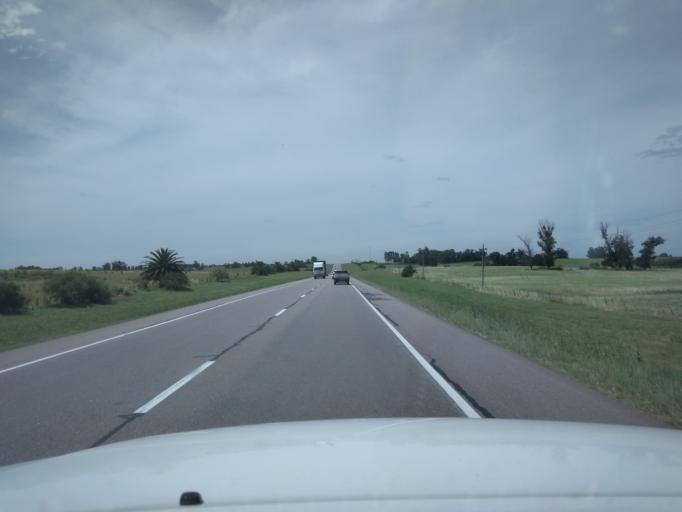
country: UY
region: Florida
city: Florida
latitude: -34.2213
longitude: -56.2092
